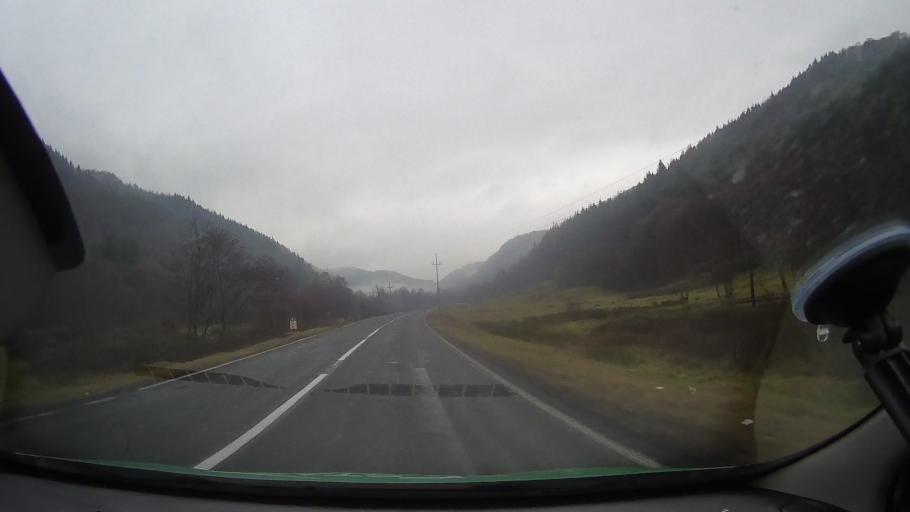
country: RO
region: Arad
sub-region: Comuna Plescuta
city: Plescuta
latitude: 46.3046
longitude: 22.4559
